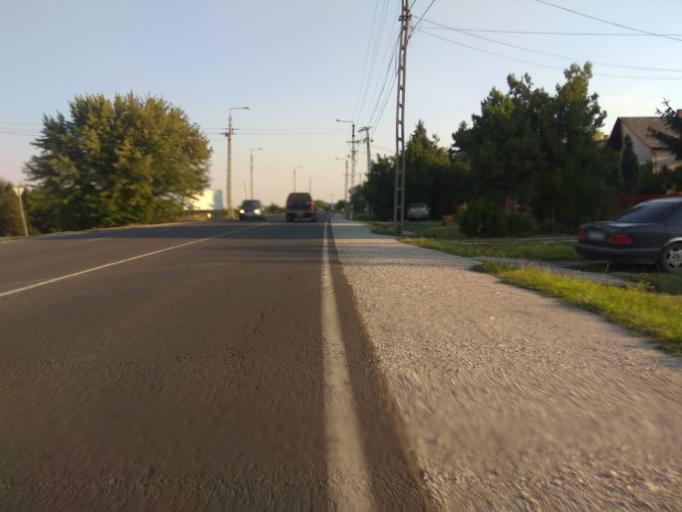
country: HU
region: Borsod-Abauj-Zemplen
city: Nyekladhaza
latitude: 47.9853
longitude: 20.8314
